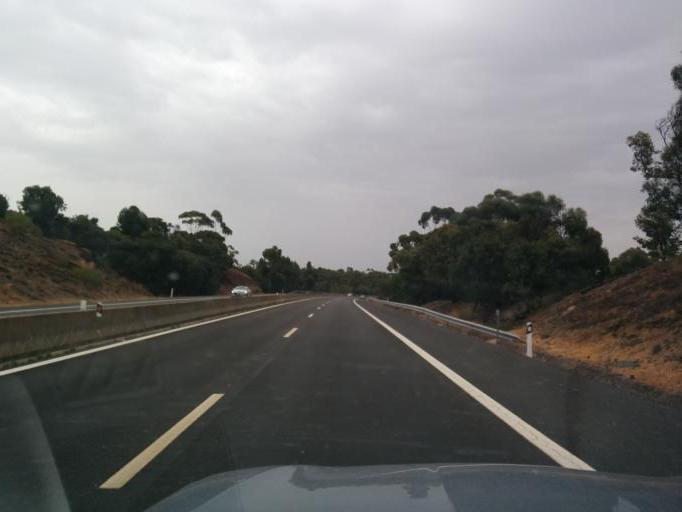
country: PT
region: Faro
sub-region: Tavira
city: Tavira
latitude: 37.1776
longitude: -7.5977
